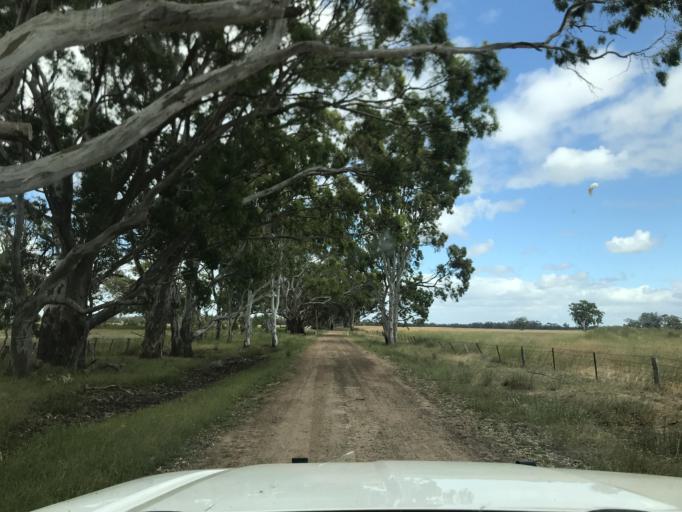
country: AU
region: South Australia
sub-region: Naracoorte and Lucindale
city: Naracoorte
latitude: -36.8987
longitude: 141.3839
